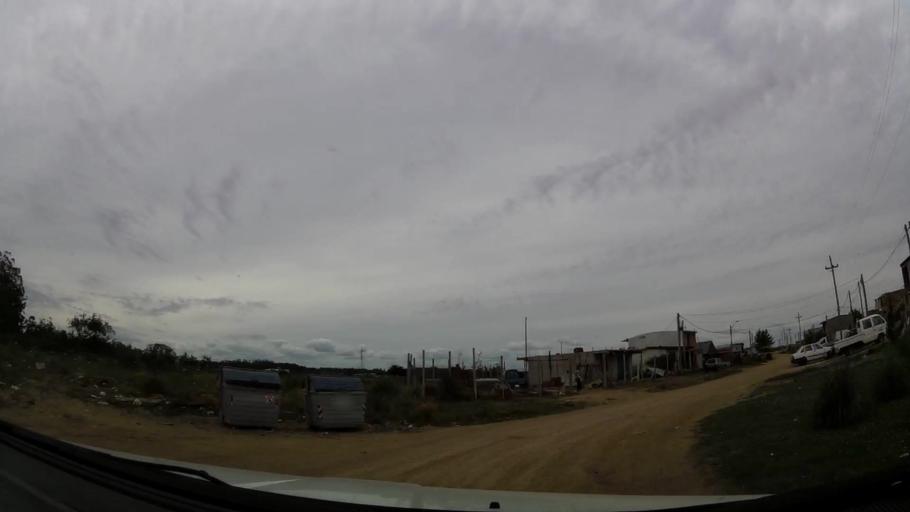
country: UY
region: Maldonado
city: Maldonado
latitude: -34.8832
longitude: -54.9421
